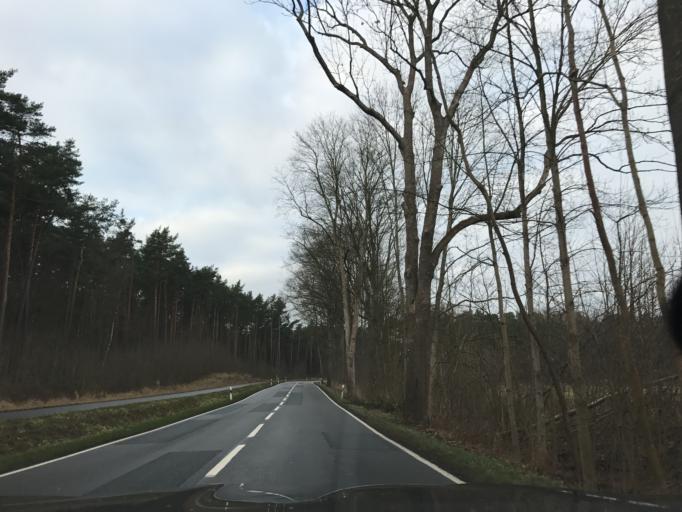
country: DE
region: Brandenburg
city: Golzow
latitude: 52.3434
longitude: 12.6417
